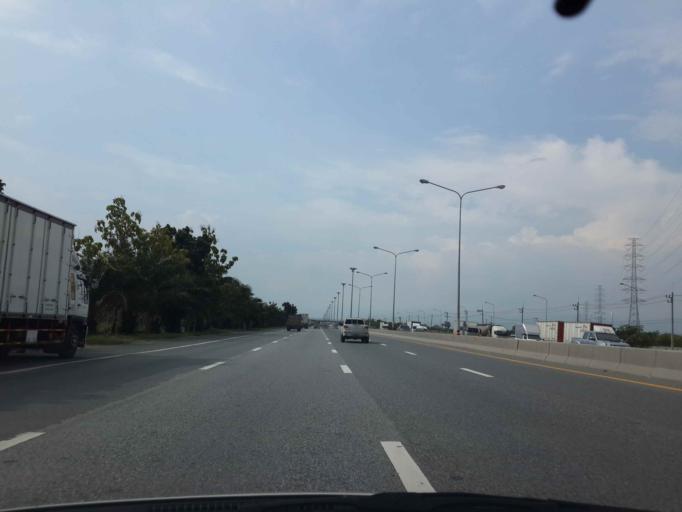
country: TH
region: Chon Buri
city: Phan Thong
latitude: 13.4500
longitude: 101.0460
